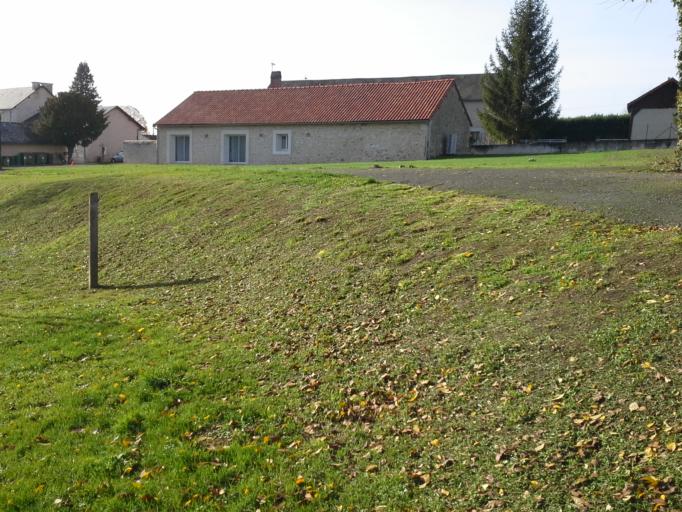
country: FR
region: Poitou-Charentes
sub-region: Departement de la Vienne
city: Pleumartin
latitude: 46.6438
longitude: 0.7542
